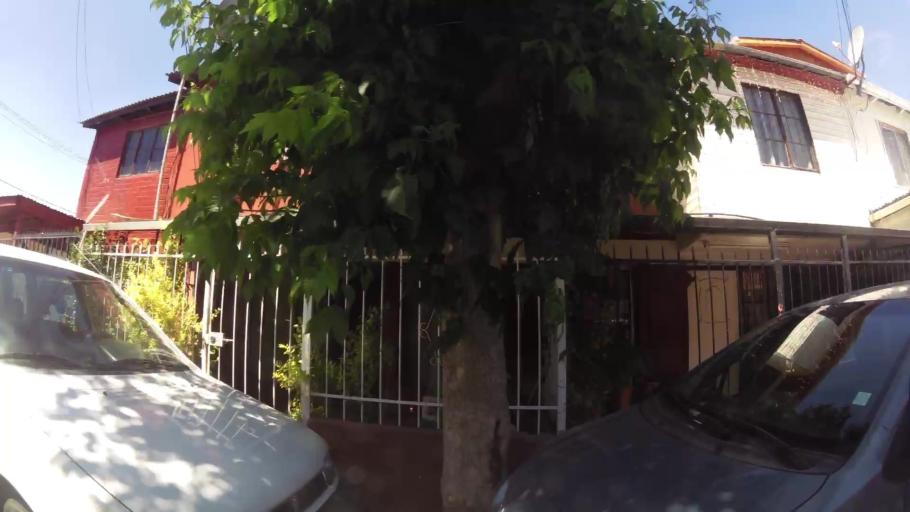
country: CL
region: Santiago Metropolitan
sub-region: Provincia de Maipo
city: San Bernardo
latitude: -33.5872
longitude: -70.6752
